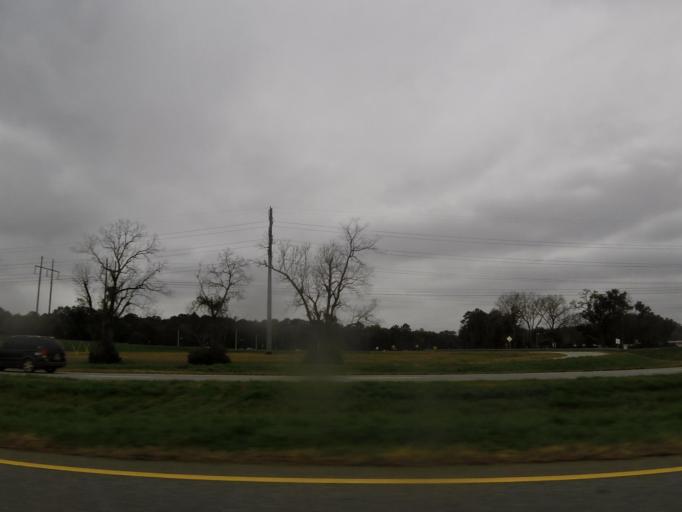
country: US
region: Georgia
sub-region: Dougherty County
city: Albany
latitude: 31.5477
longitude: -84.1152
